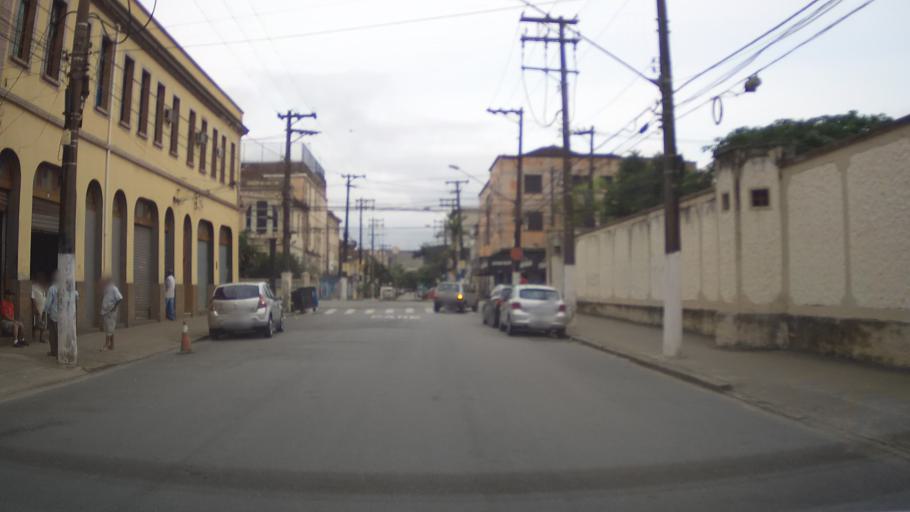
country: BR
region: Sao Paulo
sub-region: Santos
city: Santos
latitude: -23.9422
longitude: -46.3219
